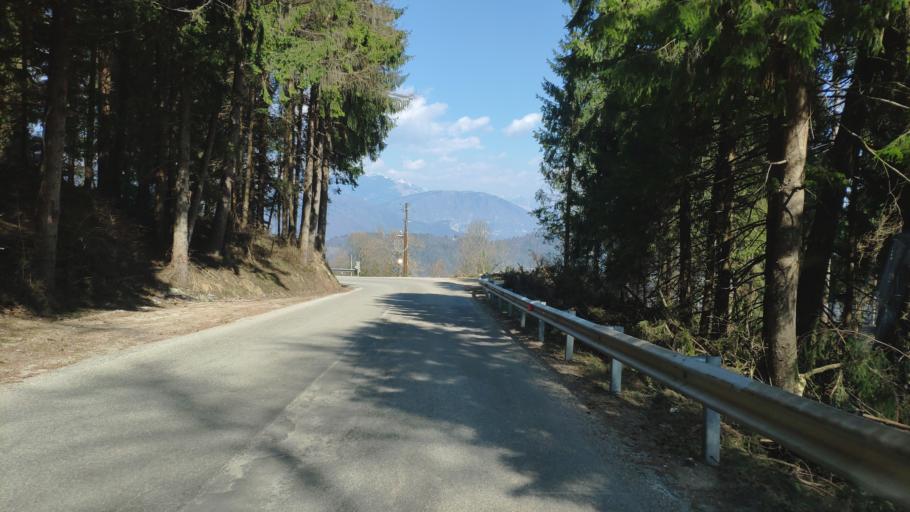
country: IT
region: Veneto
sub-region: Provincia di Vicenza
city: Enego
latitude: 45.9339
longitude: 11.7019
